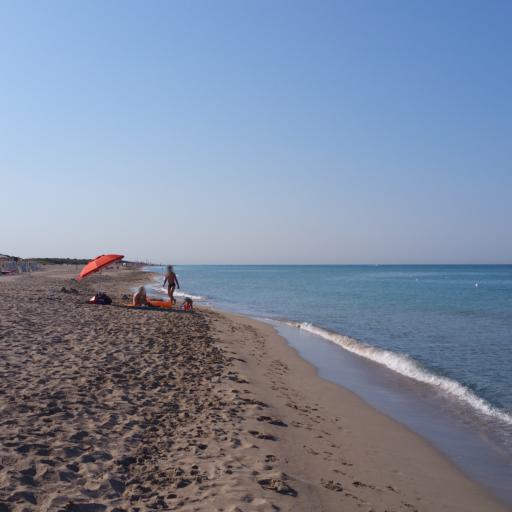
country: IT
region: Apulia
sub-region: Provincia di Lecce
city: Torre San Giovanni
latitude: 39.8730
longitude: 18.1361
